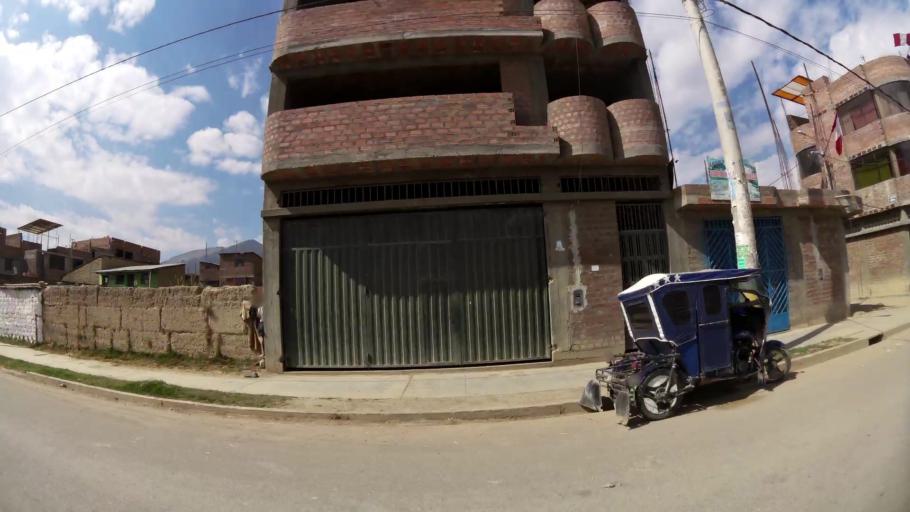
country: PE
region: Junin
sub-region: Provincia de Huancayo
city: Huancayo
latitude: -12.0916
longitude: -75.2015
